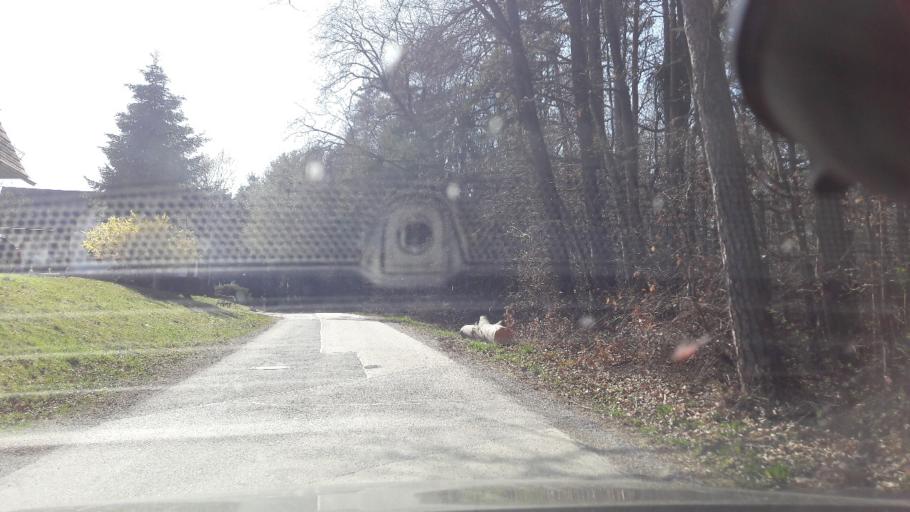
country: AT
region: Styria
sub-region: Politischer Bezirk Graz-Umgebung
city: Hitzendorf
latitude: 47.0373
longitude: 15.3174
